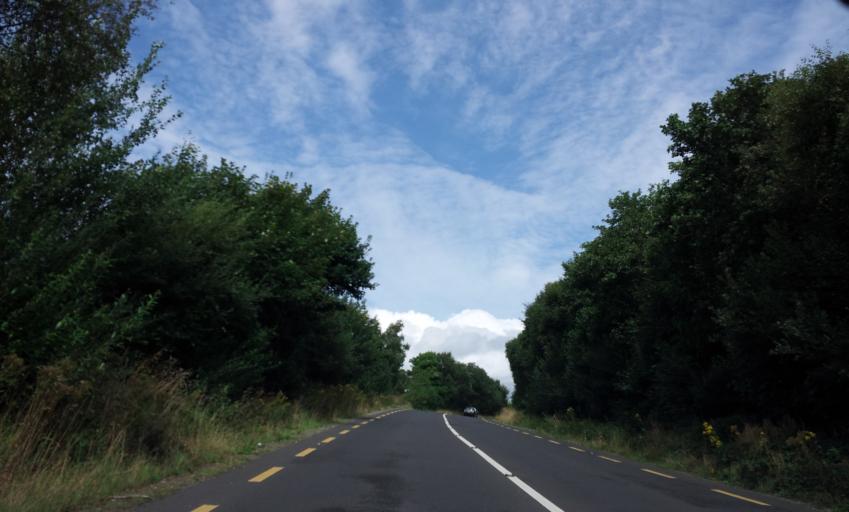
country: IE
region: Munster
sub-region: Ciarrai
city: Killorglin
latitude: 52.1012
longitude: -9.8247
